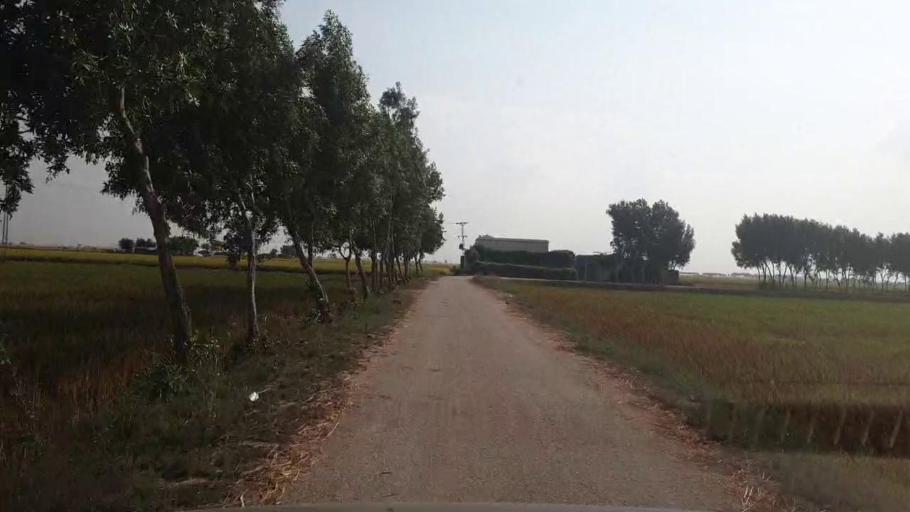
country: PK
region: Sindh
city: Kario
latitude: 24.6353
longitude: 68.5580
